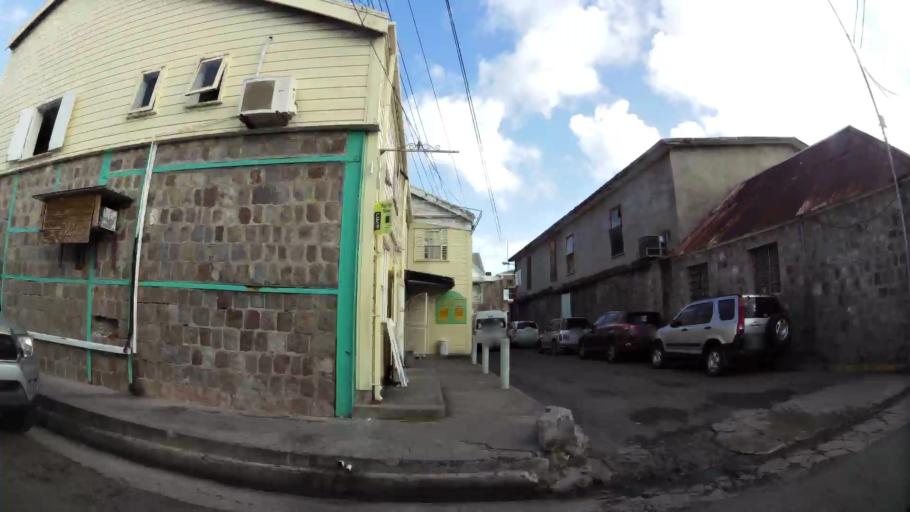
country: KN
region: Saint Paul Charlestown
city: Charlestown
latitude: 17.1385
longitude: -62.6294
